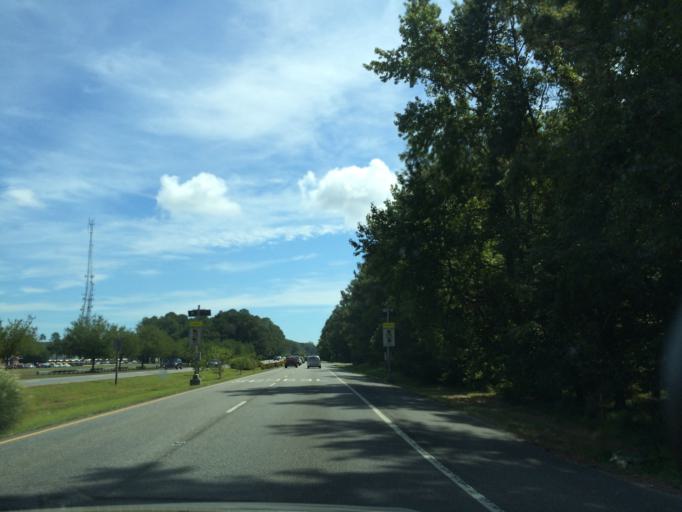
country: US
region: Virginia
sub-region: York County
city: Yorktown
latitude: 37.2038
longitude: -76.5037
